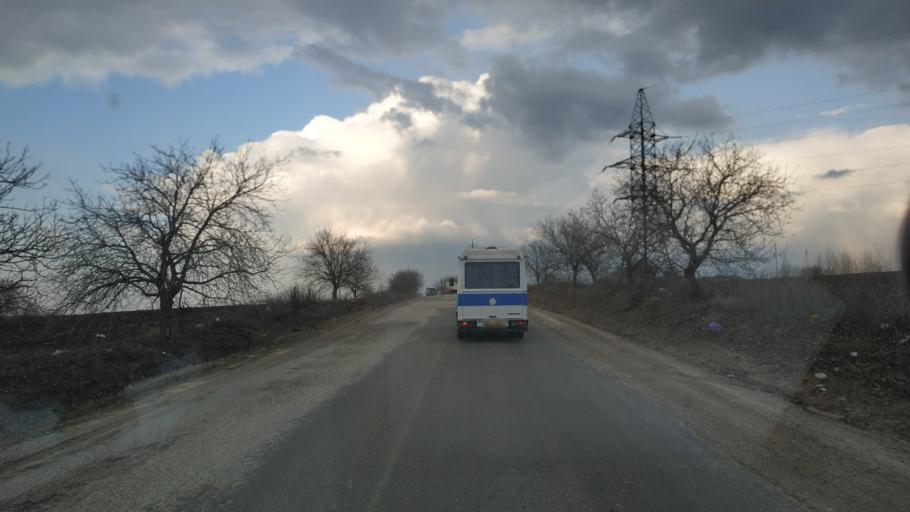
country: MD
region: Anenii Noi
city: Anenii Noi
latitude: 46.9612
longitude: 29.2844
